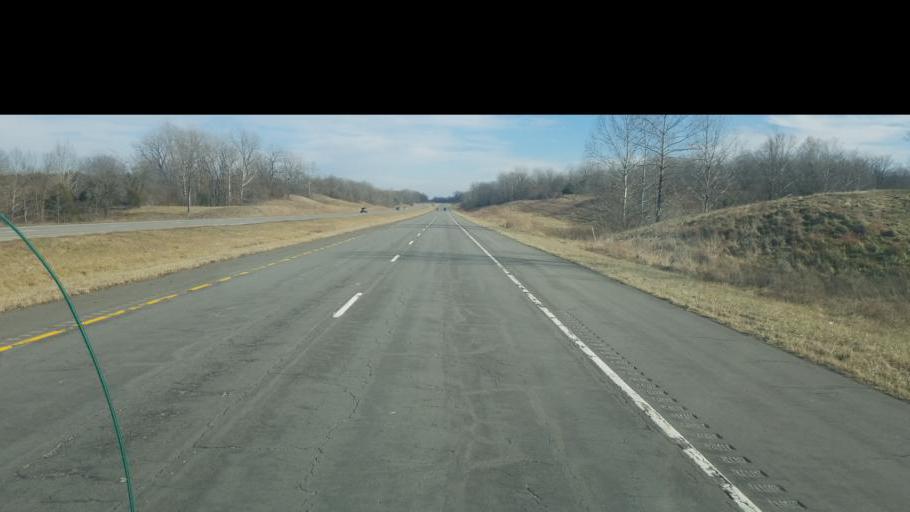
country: US
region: Illinois
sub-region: Saline County
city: Carrier Mills
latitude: 37.7304
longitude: -88.7621
